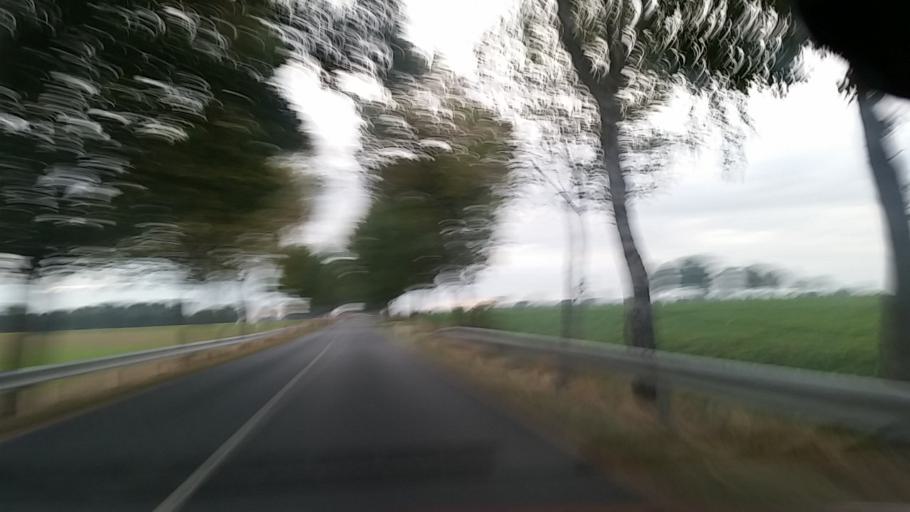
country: DE
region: Lower Saxony
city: Hankensbuttel
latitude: 52.7337
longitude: 10.5843
